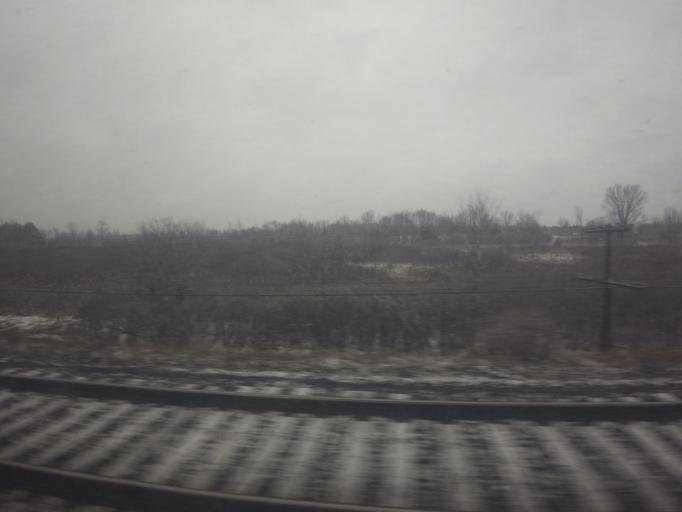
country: US
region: New York
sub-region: Jefferson County
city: Alexandria Bay
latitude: 44.4873
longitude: -75.8772
